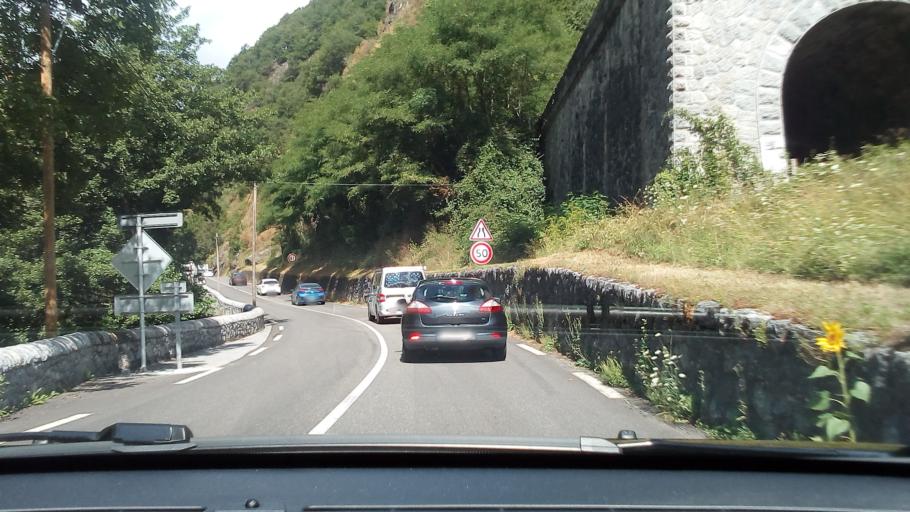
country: FR
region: Aquitaine
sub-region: Departement des Pyrenees-Atlantiques
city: Laruns
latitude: 42.9387
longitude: -0.5933
